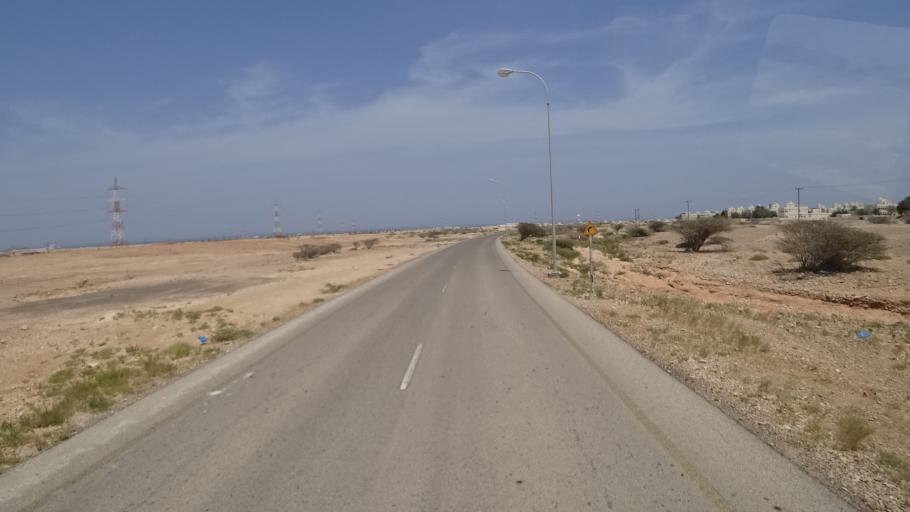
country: OM
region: Ash Sharqiyah
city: Sur
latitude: 22.6099
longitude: 59.4364
